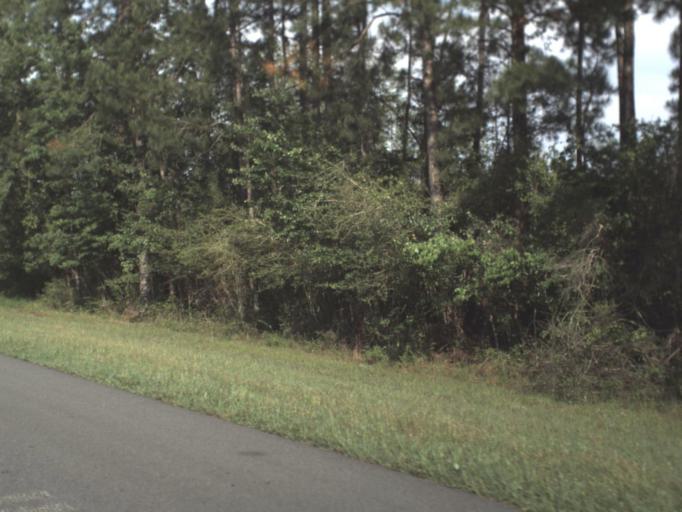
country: US
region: Florida
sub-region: Holmes County
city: Bonifay
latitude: 30.7408
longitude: -85.8780
